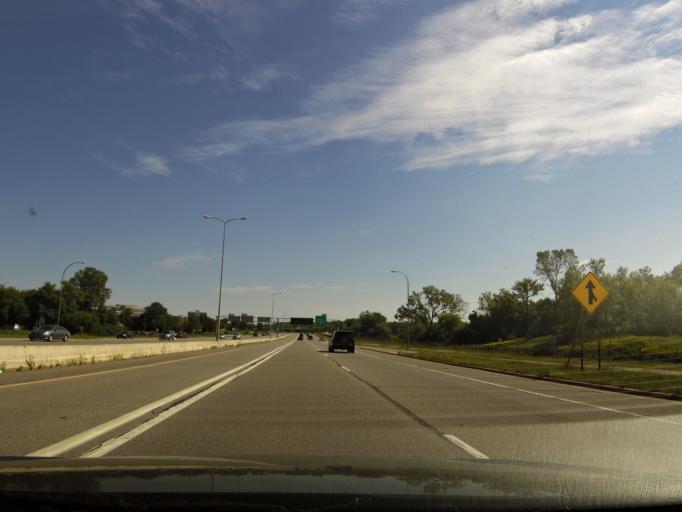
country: US
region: Minnesota
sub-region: Hennepin County
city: Minnetonka Mills
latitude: 44.9709
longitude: -93.4305
